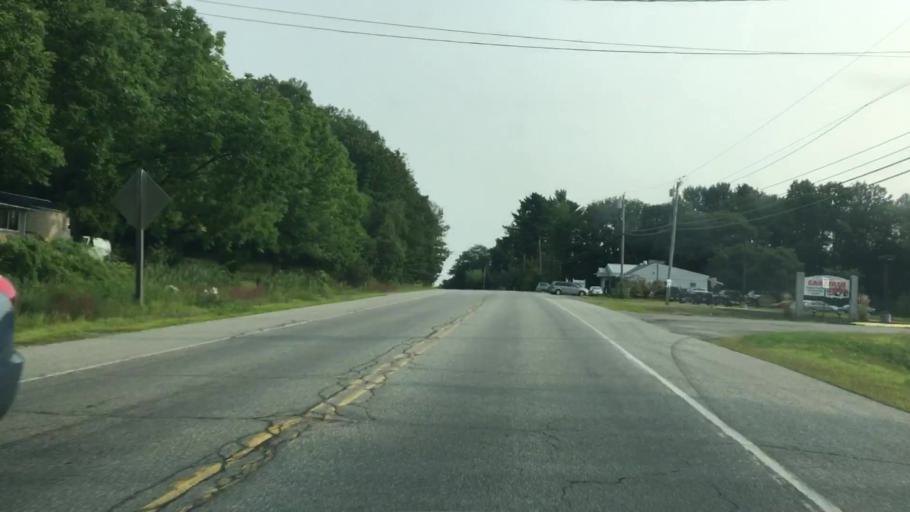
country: US
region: Maine
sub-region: Kennebec County
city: Gardiner
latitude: 44.2108
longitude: -69.7853
